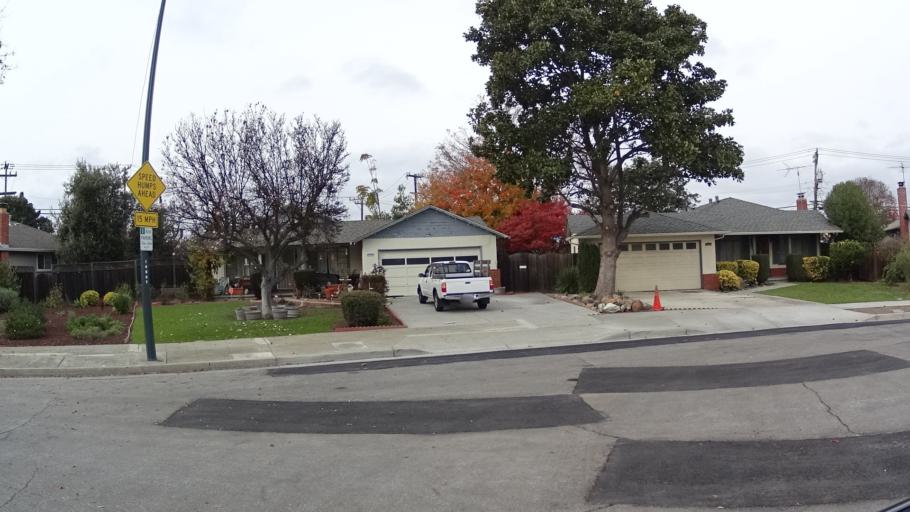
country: US
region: California
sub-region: Santa Clara County
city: Sunnyvale
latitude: 37.3708
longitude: -122.0498
